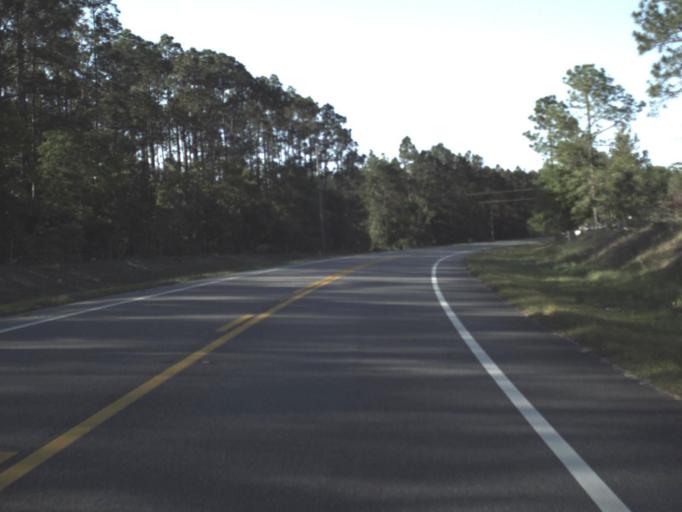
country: US
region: Florida
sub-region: Liberty County
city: Bristol
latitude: 30.4147
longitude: -84.7844
